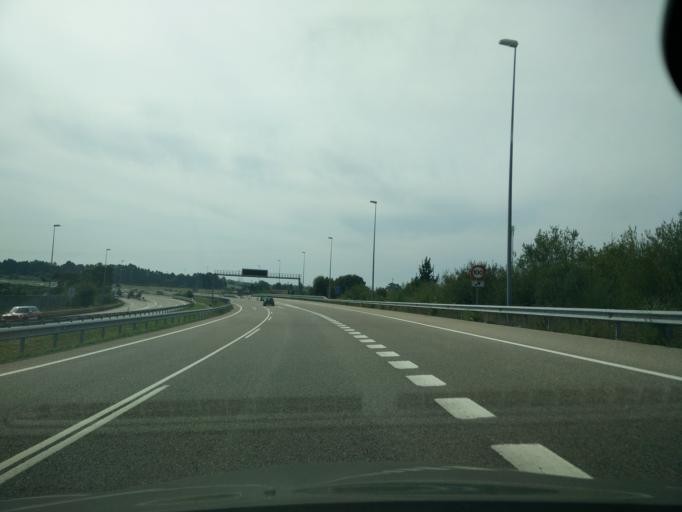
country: ES
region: Asturias
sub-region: Province of Asturias
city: Arriba
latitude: 43.5121
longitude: -5.5655
